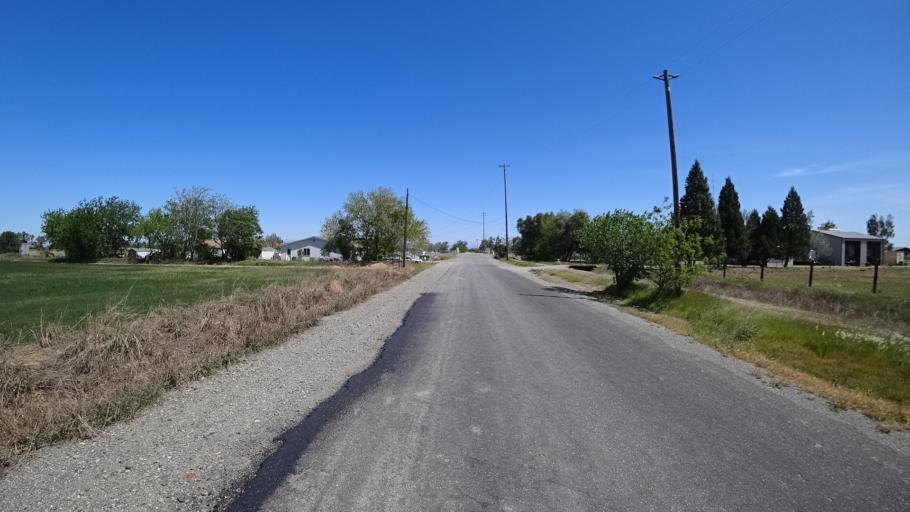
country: US
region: California
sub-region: Glenn County
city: Orland
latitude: 39.7397
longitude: -122.1560
